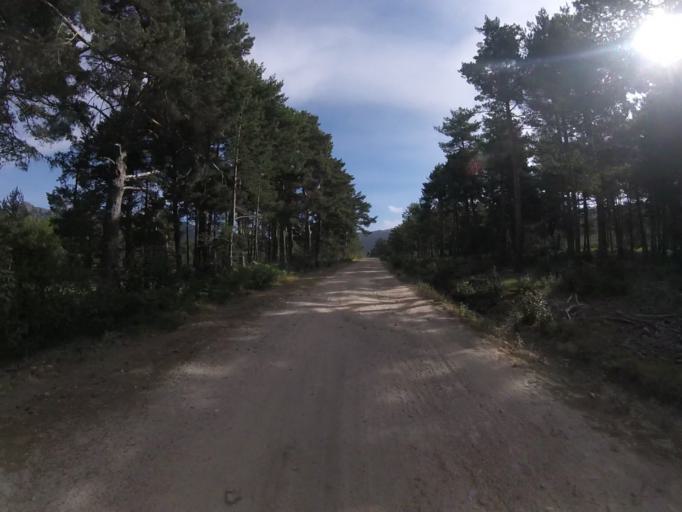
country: ES
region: Castille and Leon
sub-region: Provincia de Avila
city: Peguerinos
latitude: 40.6604
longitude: -4.1840
